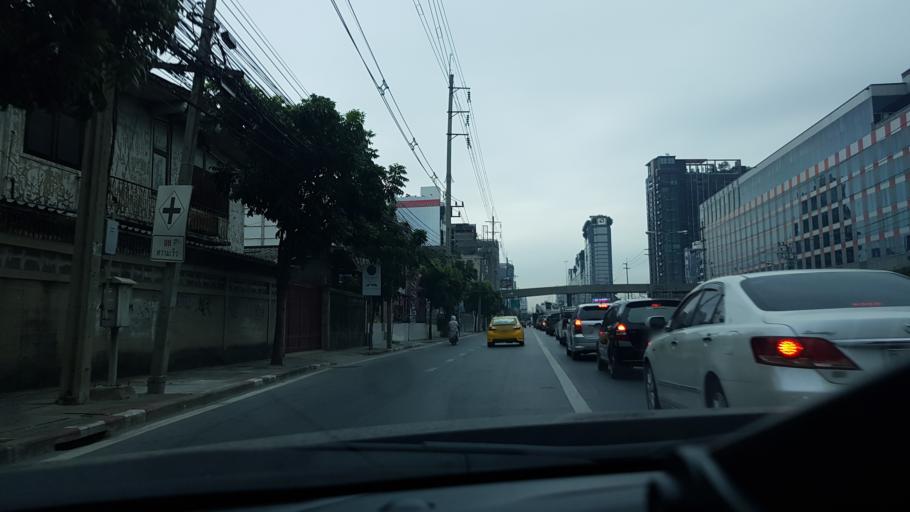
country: TH
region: Bangkok
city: Chatuchak
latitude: 13.8096
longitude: 100.5754
